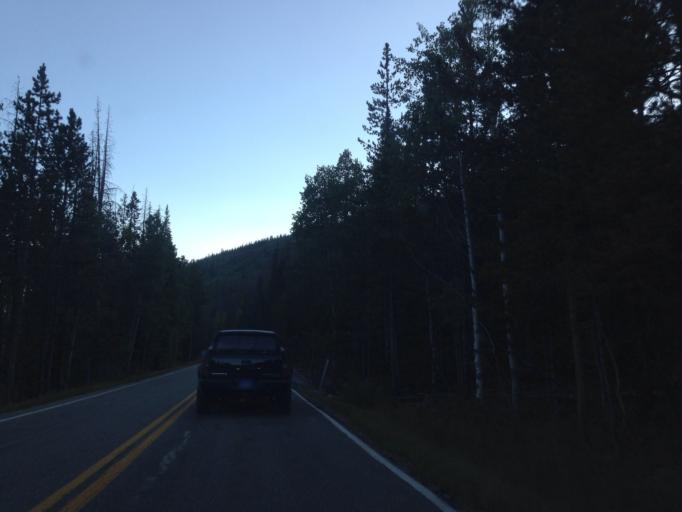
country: US
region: Utah
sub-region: Summit County
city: Francis
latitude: 40.6247
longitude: -110.9614
